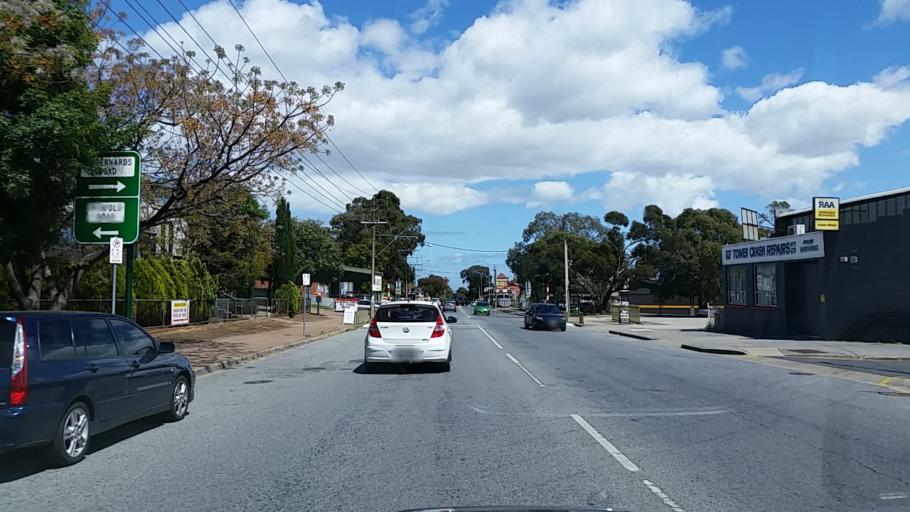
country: AU
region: South Australia
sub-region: Burnside
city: Wattle Park
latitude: -34.9129
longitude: 138.6782
